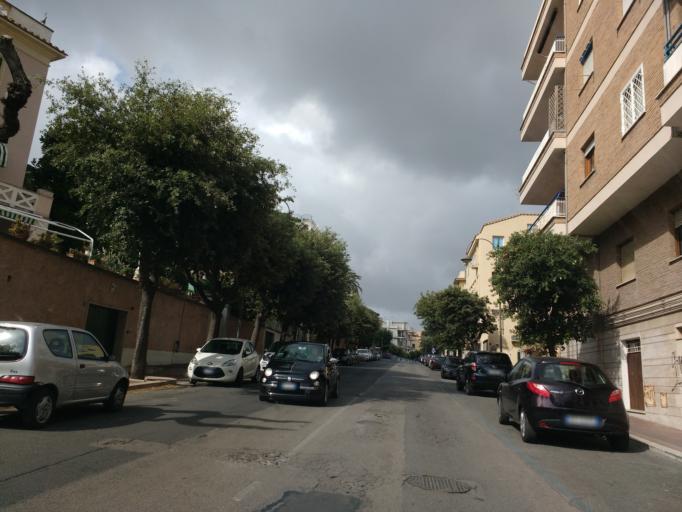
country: IT
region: Latium
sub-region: Citta metropolitana di Roma Capitale
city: Anzio
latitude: 41.4503
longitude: 12.6323
